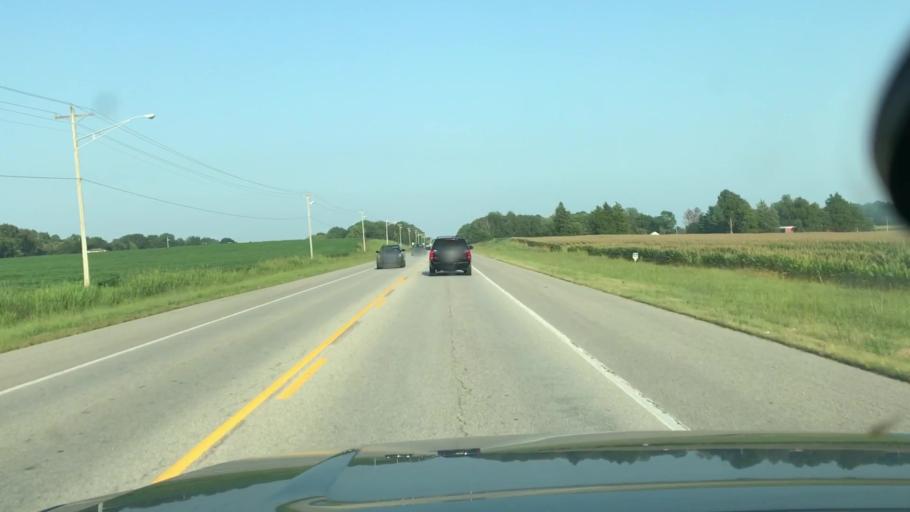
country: US
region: Tennessee
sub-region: Sumner County
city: Portland
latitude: 36.5787
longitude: -86.5391
